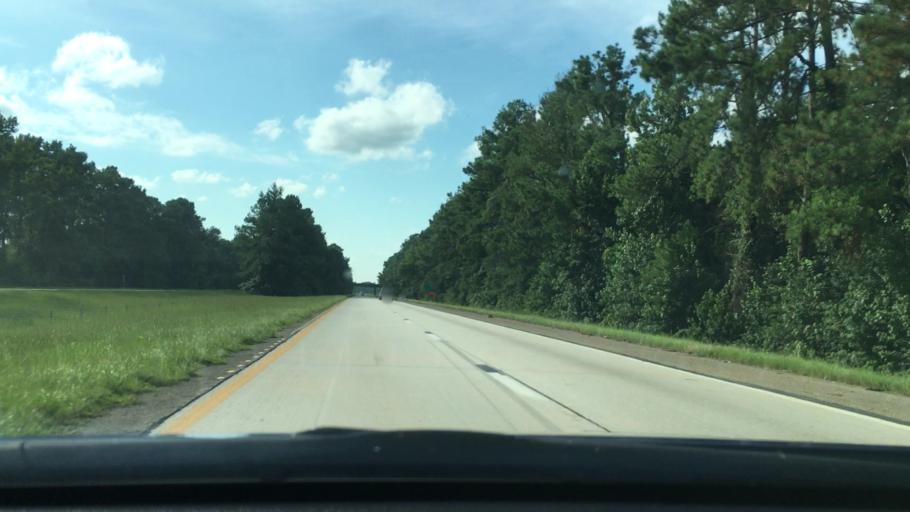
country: US
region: South Carolina
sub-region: Orangeburg County
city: Holly Hill
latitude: 33.2515
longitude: -80.4692
